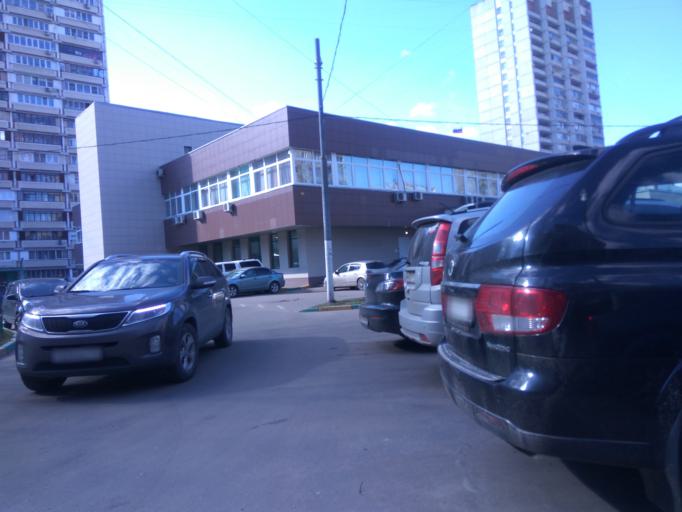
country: RU
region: Moscow
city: Ivanovskoye
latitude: 55.7667
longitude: 37.8351
